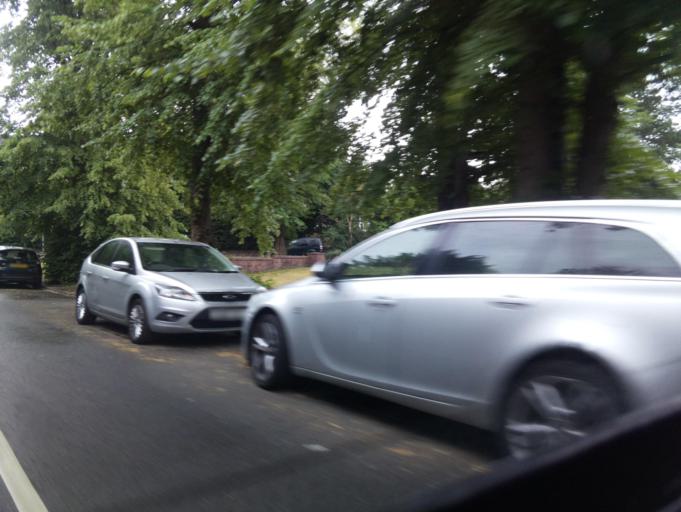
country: GB
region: England
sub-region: Surrey
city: Redhill
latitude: 51.2380
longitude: -0.1849
